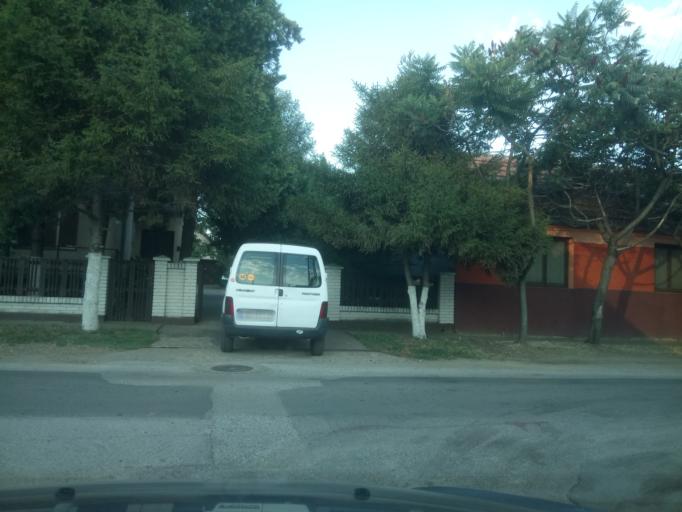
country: RS
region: Autonomna Pokrajina Vojvodina
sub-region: Sremski Okrug
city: Ingija
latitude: 45.0562
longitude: 20.0772
